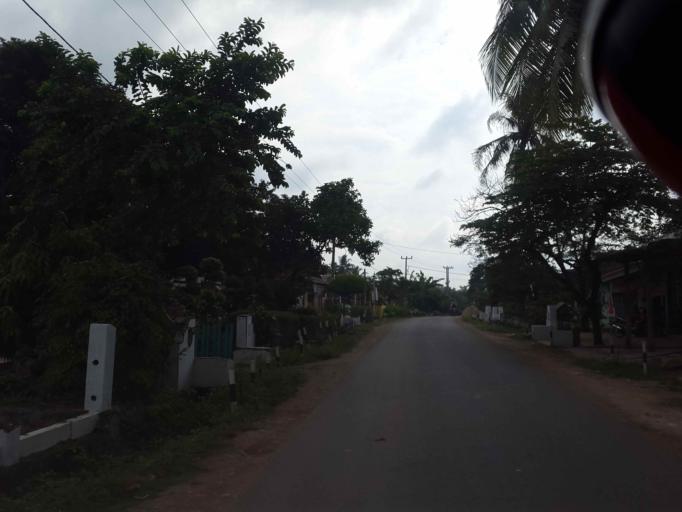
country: ID
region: Lampung
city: Natar
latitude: -5.3071
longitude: 105.2198
